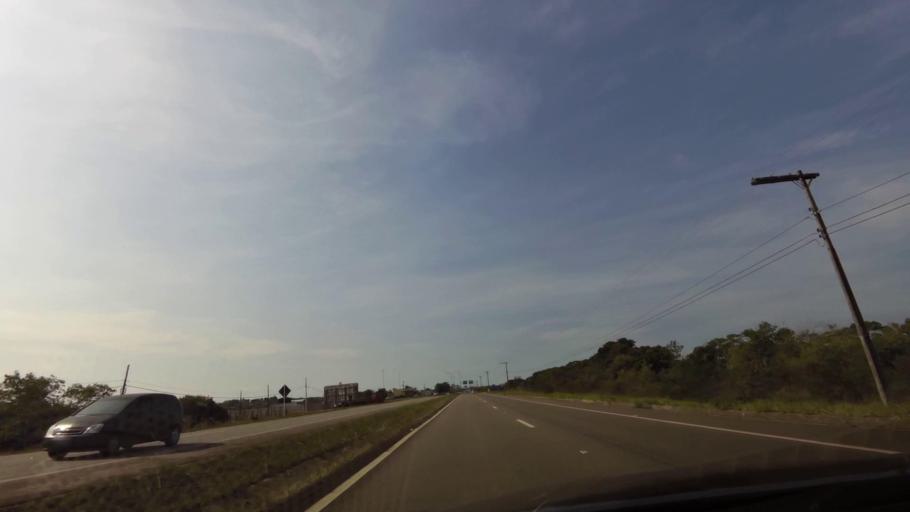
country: BR
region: Espirito Santo
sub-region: Guarapari
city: Guarapari
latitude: -20.5506
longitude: -40.3991
